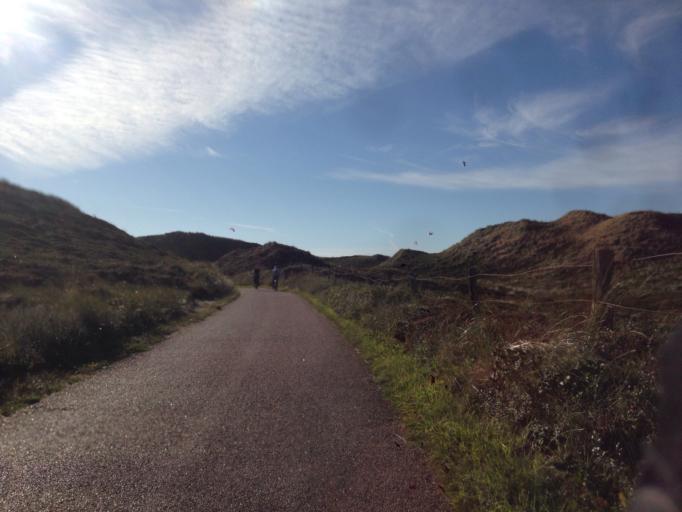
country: DE
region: Schleswig-Holstein
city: List
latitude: 55.0027
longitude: 8.3693
